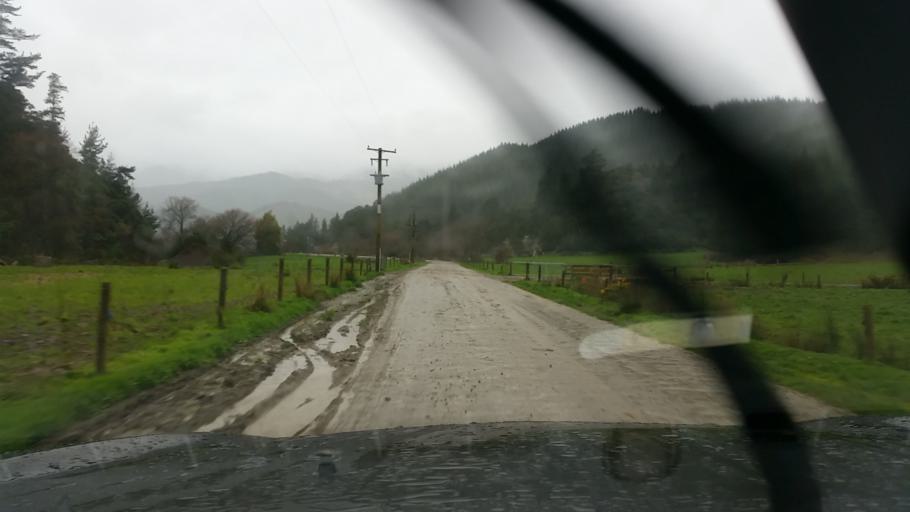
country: NZ
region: Marlborough
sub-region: Marlborough District
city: Picton
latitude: -41.3563
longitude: 173.9285
